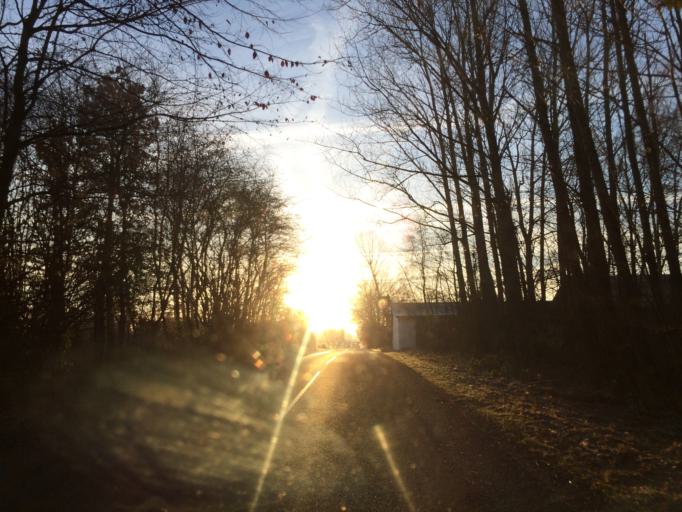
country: DK
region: South Denmark
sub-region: Odense Kommune
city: Bellinge
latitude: 55.2871
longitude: 10.2924
